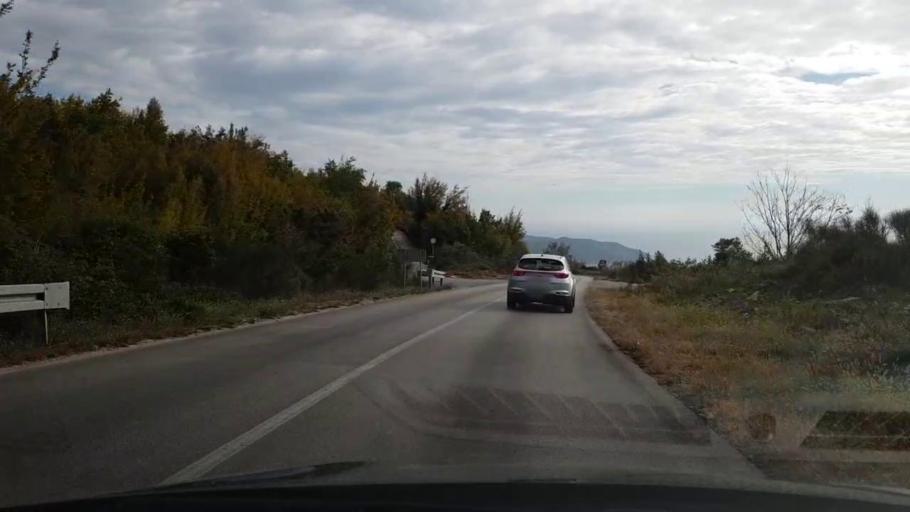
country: ME
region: Herceg Novi
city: Herceg-Novi
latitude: 42.4710
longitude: 18.5372
